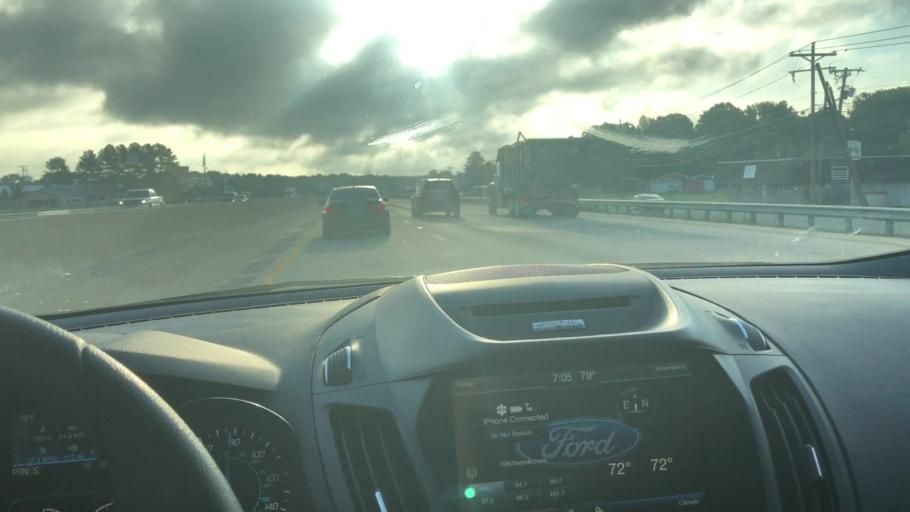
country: US
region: Arkansas
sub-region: Pulaski County
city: Alexander
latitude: 34.6420
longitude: -92.4410
